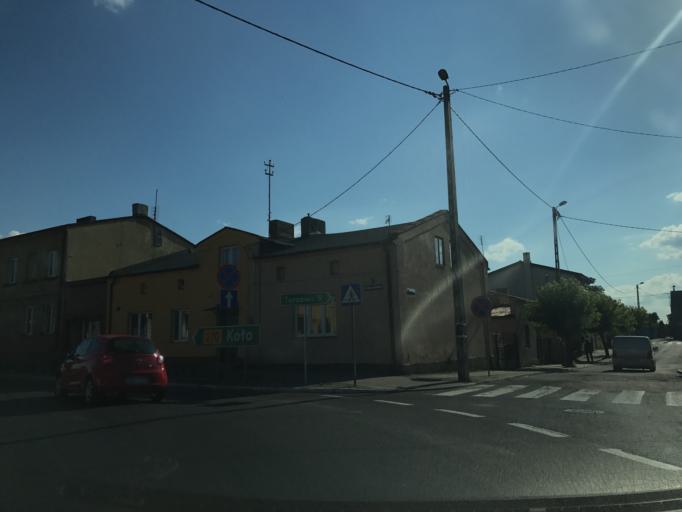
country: PL
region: Kujawsko-Pomorskie
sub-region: Powiat wloclawski
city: Lubraniec
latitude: 52.5415
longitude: 18.8319
